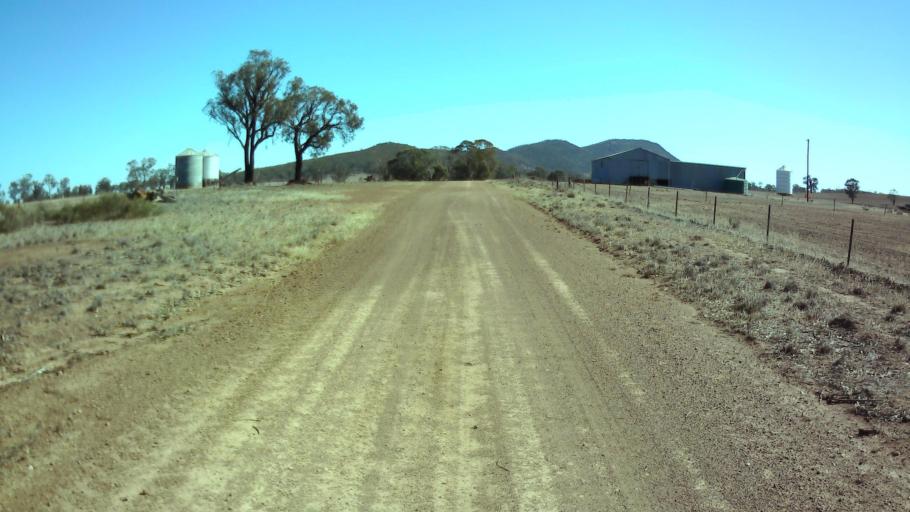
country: AU
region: New South Wales
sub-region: Weddin
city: Grenfell
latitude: -33.7693
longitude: 147.9233
